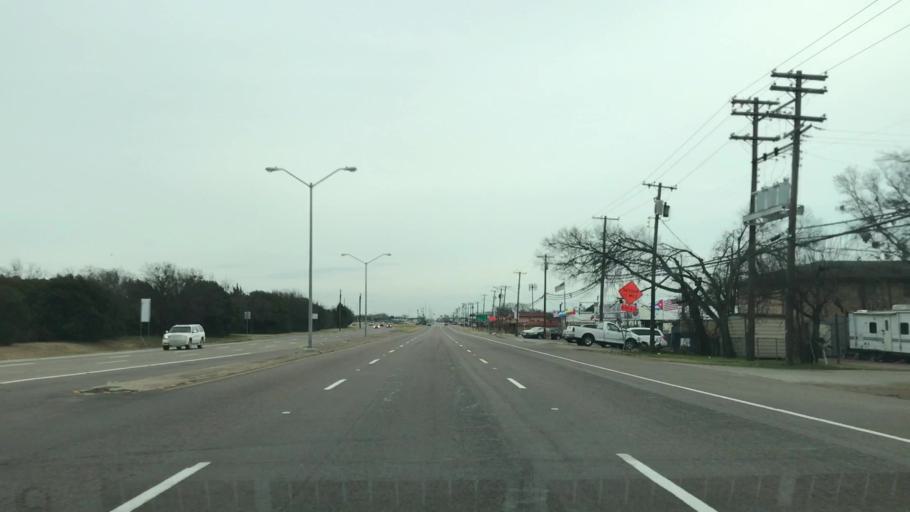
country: US
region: Texas
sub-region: Dallas County
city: Cockrell Hill
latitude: 32.7496
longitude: -96.8853
